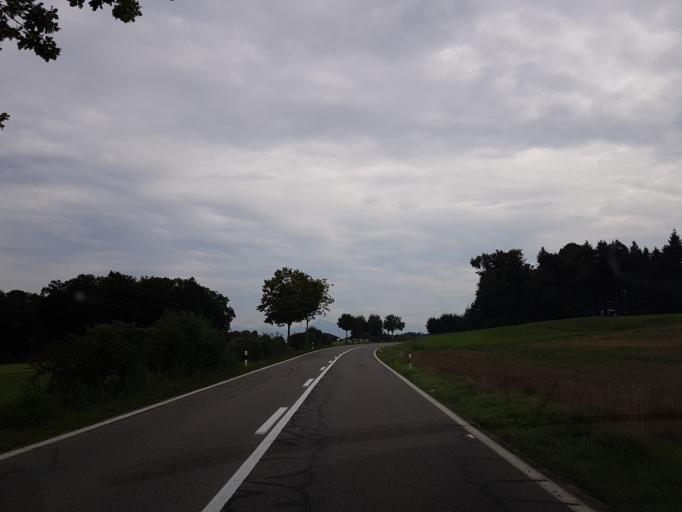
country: CH
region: Aargau
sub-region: Bezirk Muri
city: Merenschwand
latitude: 47.2579
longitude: 8.3546
